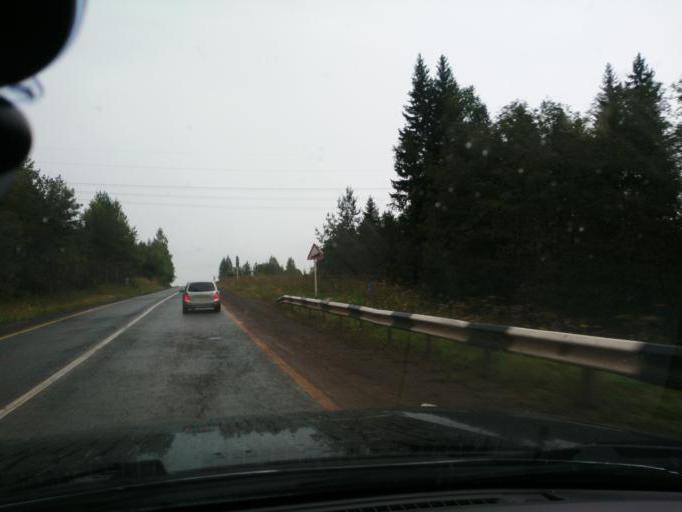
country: RU
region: Perm
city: Barda
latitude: 56.8922
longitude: 55.7511
